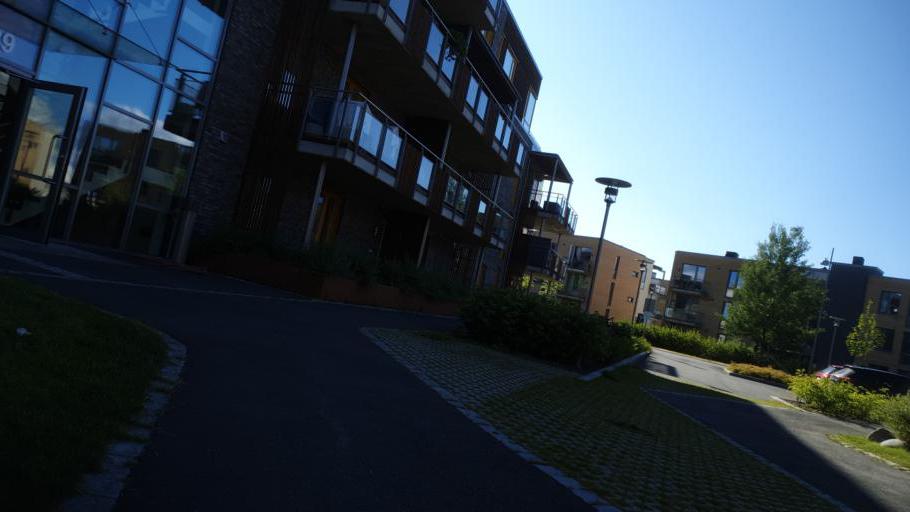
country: NO
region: Sor-Trondelag
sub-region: Trondheim
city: Trondheim
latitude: 63.4349
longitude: 10.5041
